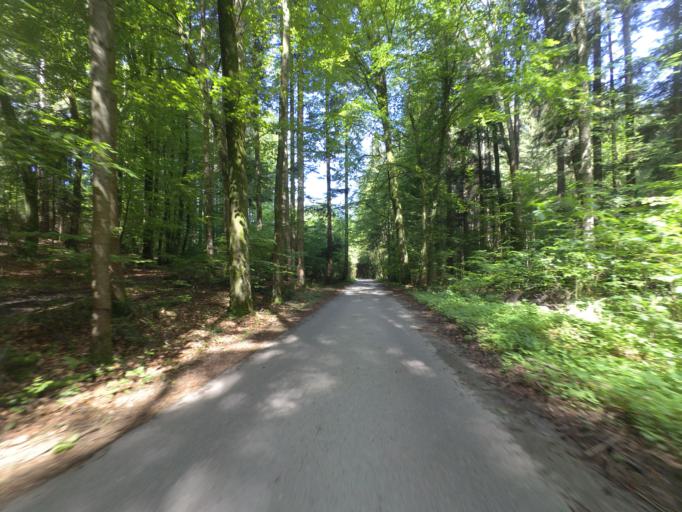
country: DE
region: Bavaria
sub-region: Upper Bavaria
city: Petting
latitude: 47.8988
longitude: 12.8134
